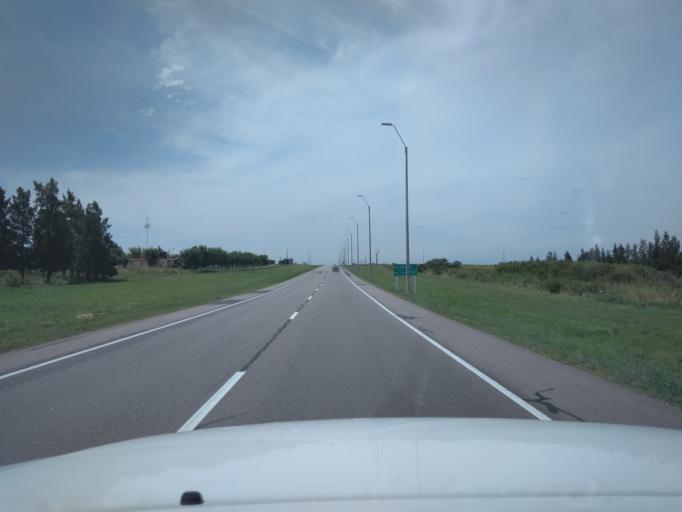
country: UY
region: Florida
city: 25 de Mayo
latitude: -34.2412
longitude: -56.2132
